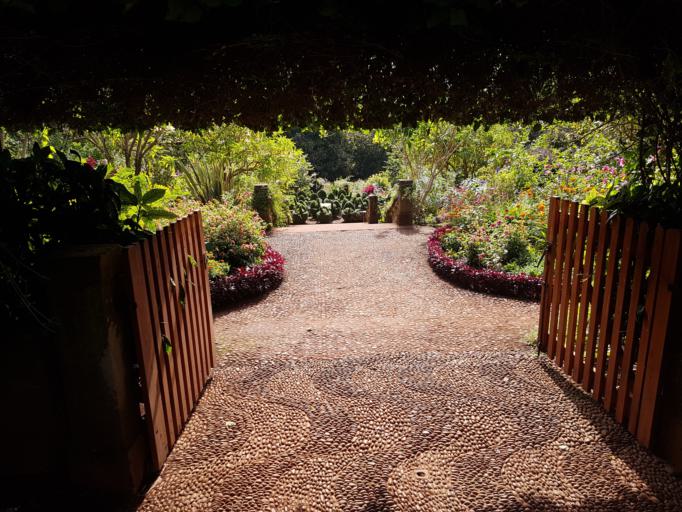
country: PT
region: Madeira
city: Canico
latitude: 32.6584
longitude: -16.8663
